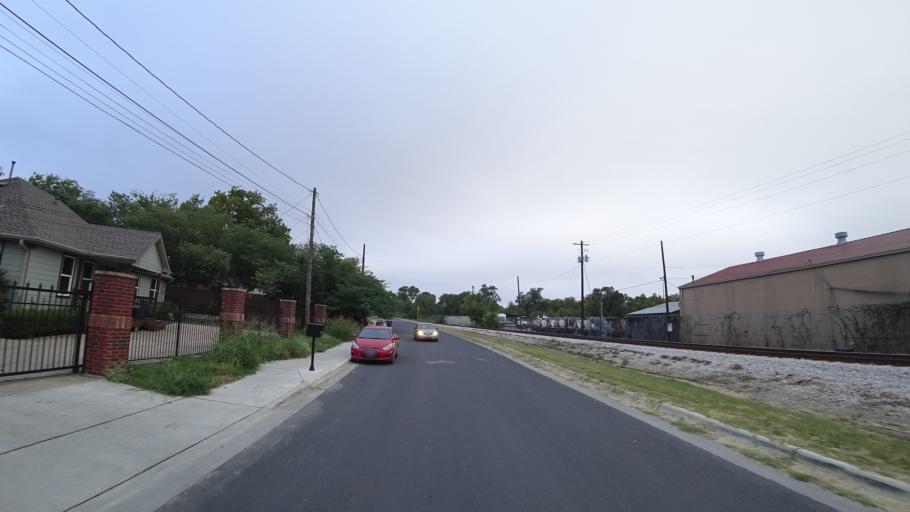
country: US
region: Texas
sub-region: Travis County
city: Austin
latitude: 30.2646
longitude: -97.7132
